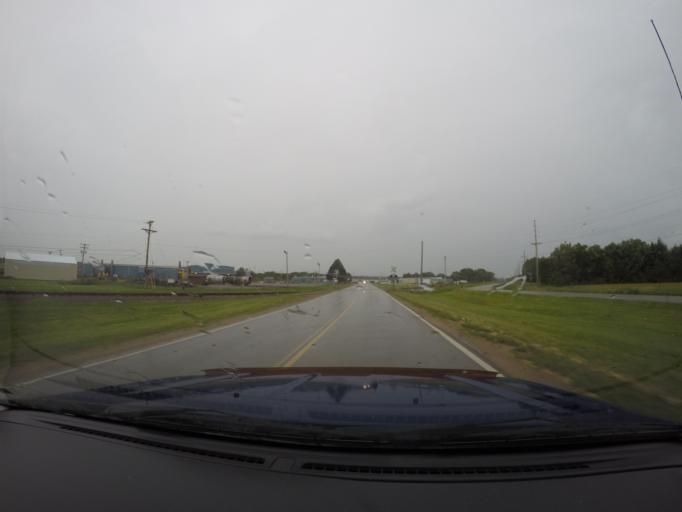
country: US
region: Kansas
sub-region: Cloud County
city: Concordia
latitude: 39.5738
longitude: -97.6319
